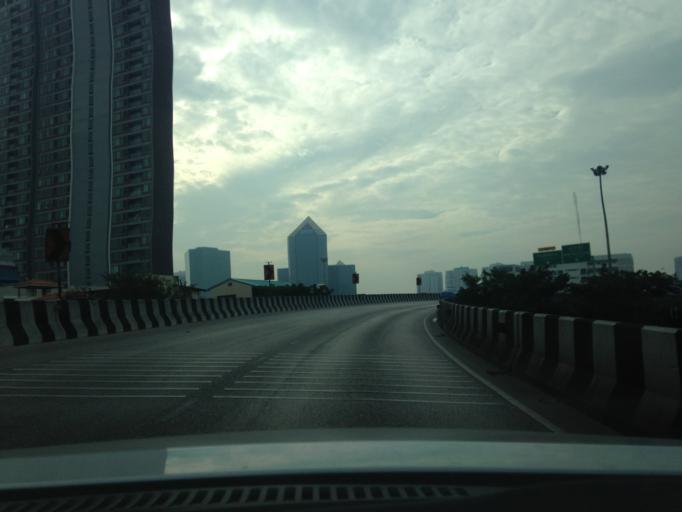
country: TH
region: Bangkok
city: Chatuchak
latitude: 13.8318
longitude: 100.5586
